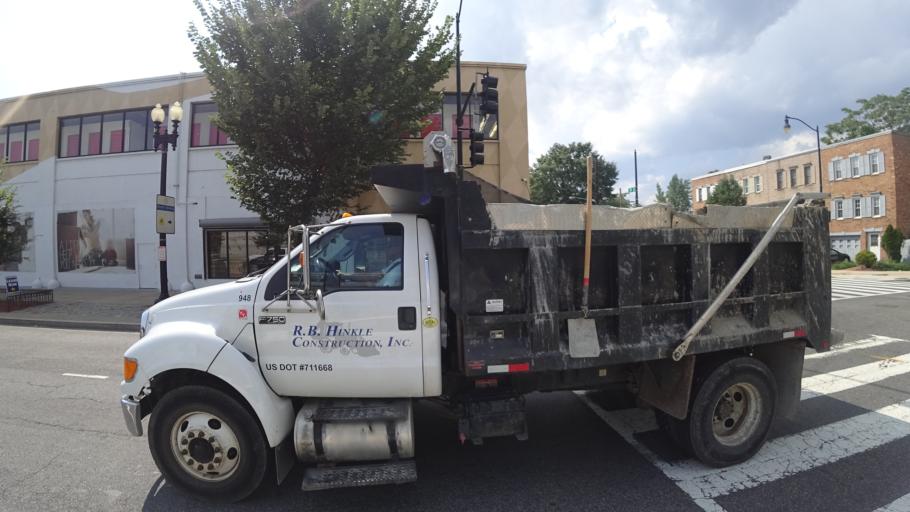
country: US
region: Washington, D.C.
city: Washington, D.C.
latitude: 38.8719
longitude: -77.0091
